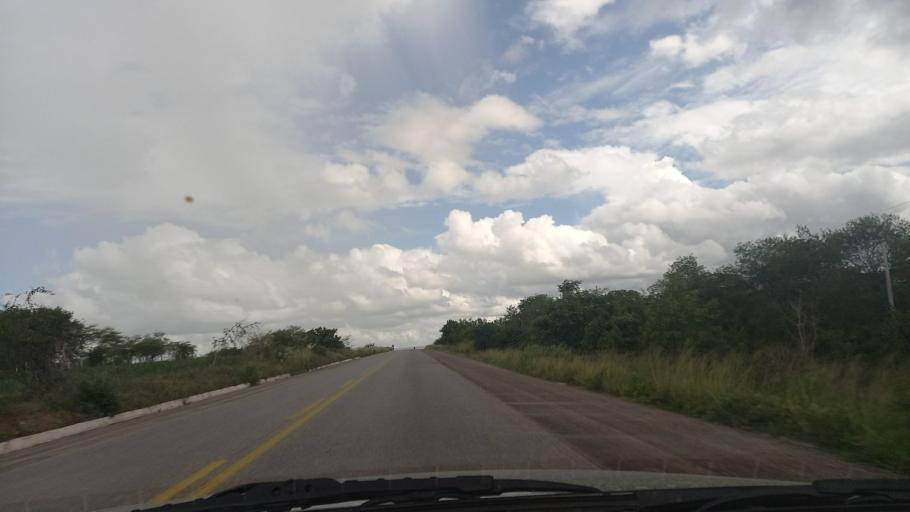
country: BR
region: Pernambuco
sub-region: Cachoeirinha
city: Cachoeirinha
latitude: -8.5441
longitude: -36.2699
